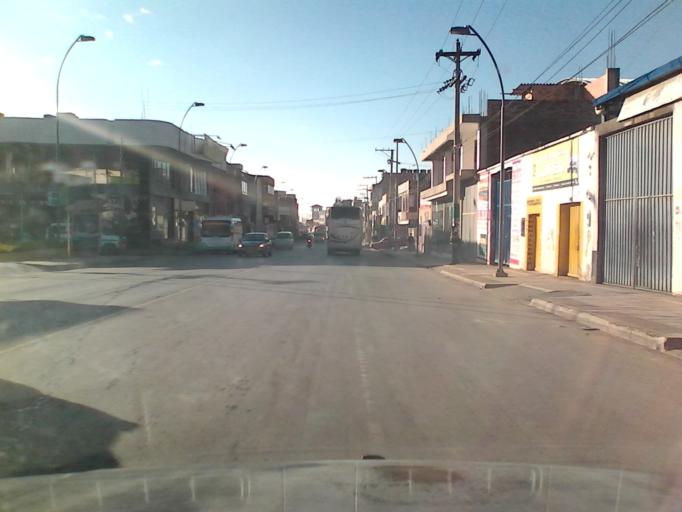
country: CO
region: Boyaca
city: Duitama
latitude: 5.8269
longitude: -73.0291
